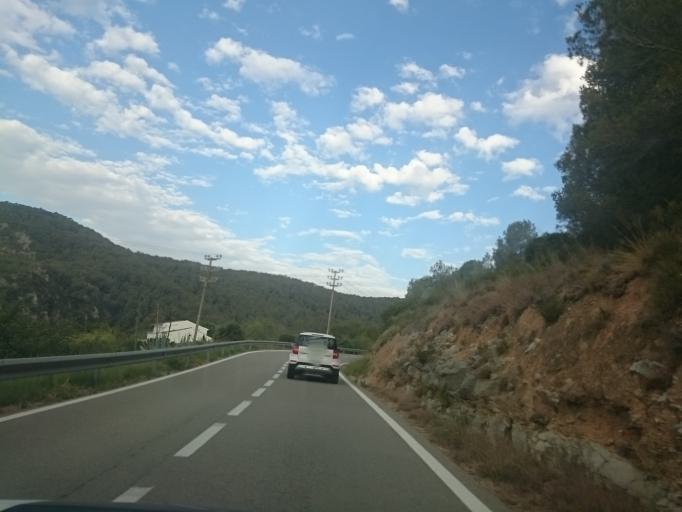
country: ES
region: Catalonia
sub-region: Provincia de Barcelona
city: Cubelles
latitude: 41.2411
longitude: 1.6621
